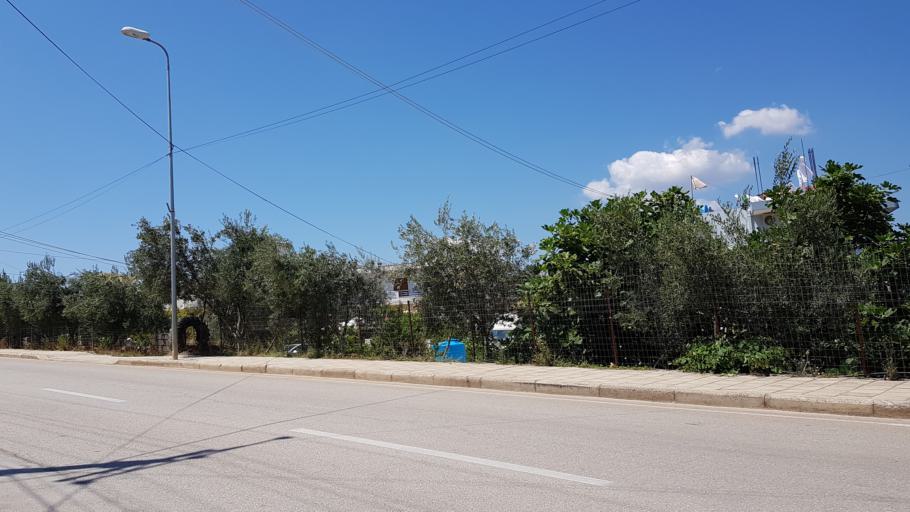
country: AL
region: Vlore
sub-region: Rrethi i Sarandes
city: Xarre
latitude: 39.7654
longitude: 20.0016
